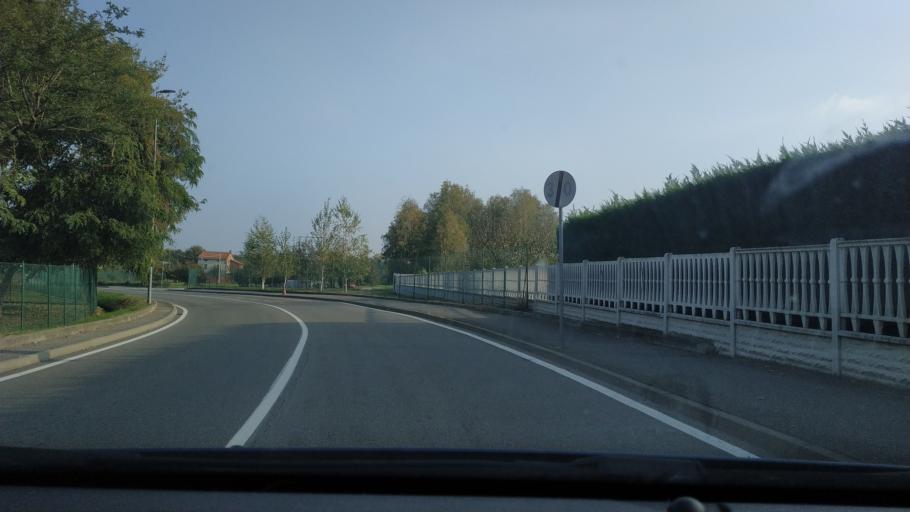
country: IT
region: Piedmont
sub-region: Provincia di Biella
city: Candelo
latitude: 45.5477
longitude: 8.0974
